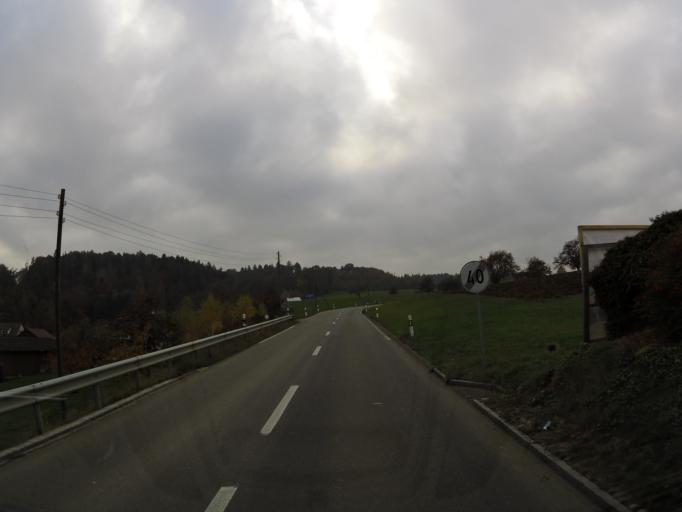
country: CH
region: Thurgau
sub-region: Kreuzlingen District
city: Tagerwilen
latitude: 47.6546
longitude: 9.1226
